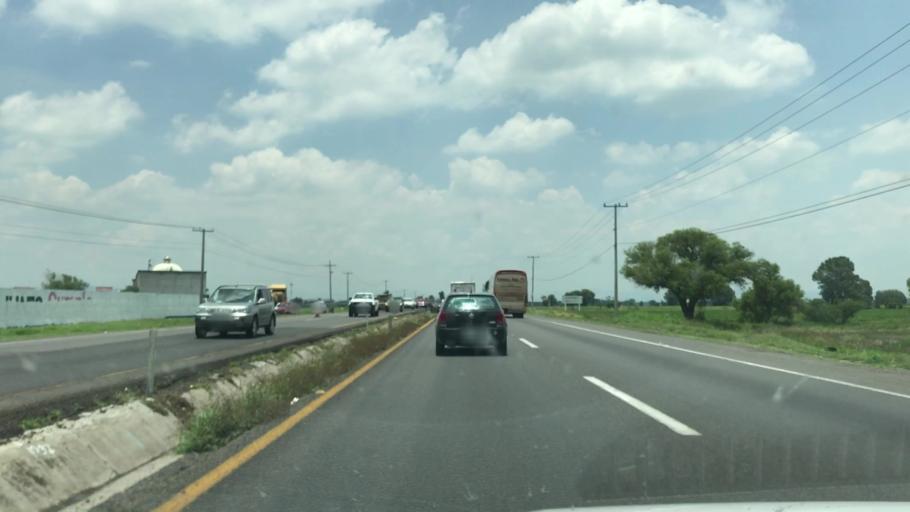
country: MX
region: Guanajuato
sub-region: Irapuato
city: Colonia Morelos de Guadalupe de Rivera
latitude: 20.5864
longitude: -101.4292
